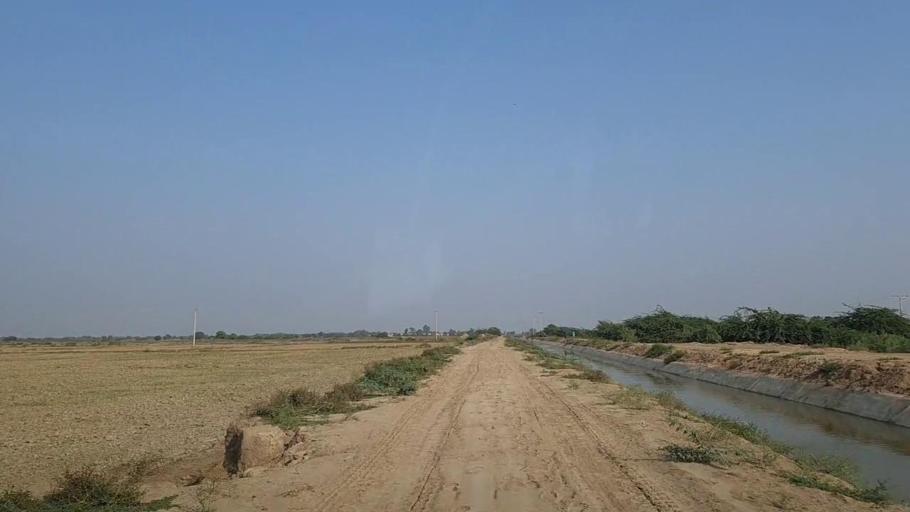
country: PK
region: Sindh
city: Mirpur Sakro
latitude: 24.6154
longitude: 67.7216
